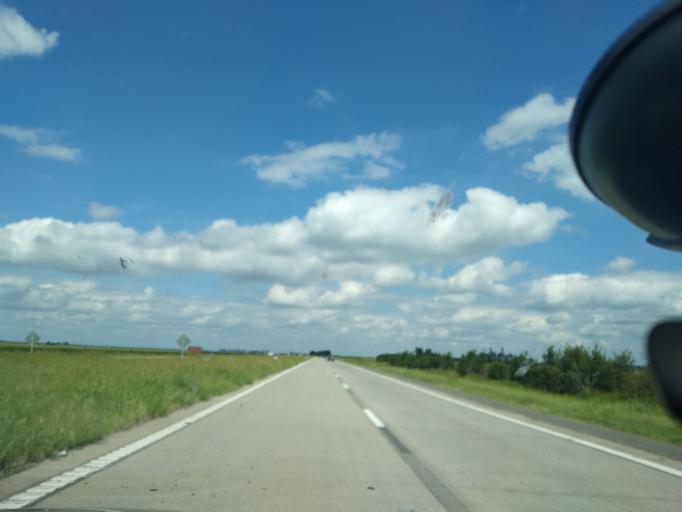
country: AR
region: Cordoba
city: Marcos Juarez
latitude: -32.6789
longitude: -62.0265
